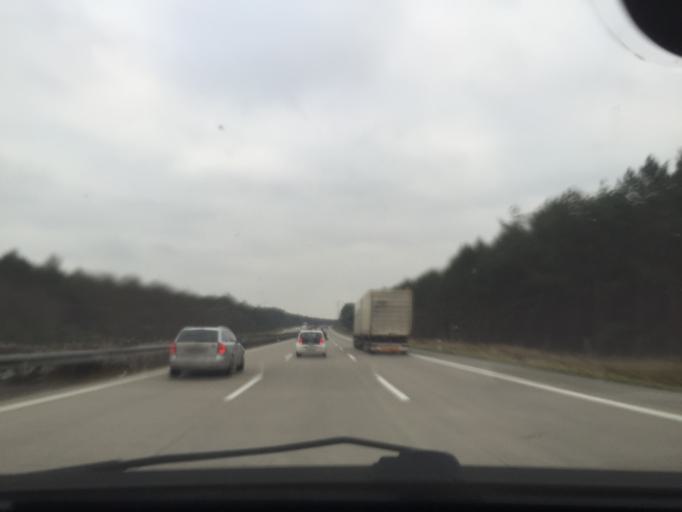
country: DE
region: Saxony-Anhalt
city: Tucheim
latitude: 52.2511
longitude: 12.2024
